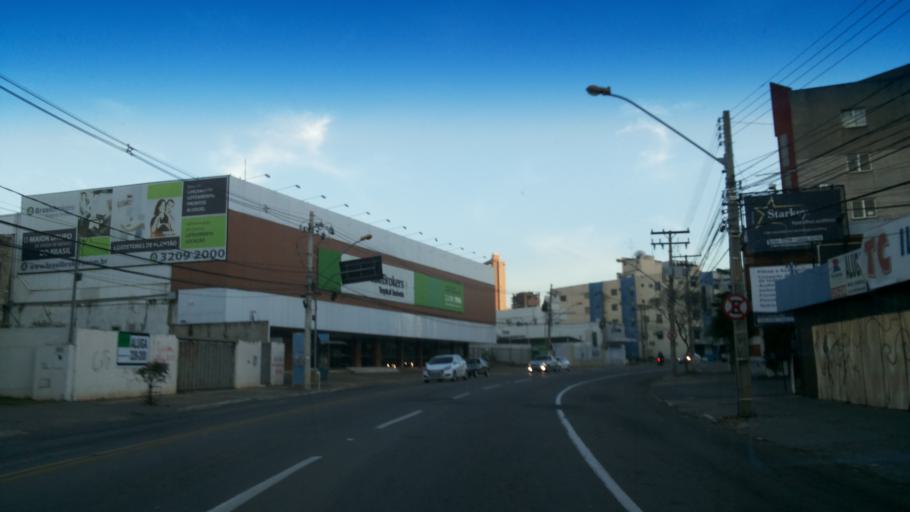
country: BR
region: Goias
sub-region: Goiania
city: Goiania
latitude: -16.6872
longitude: -49.2597
